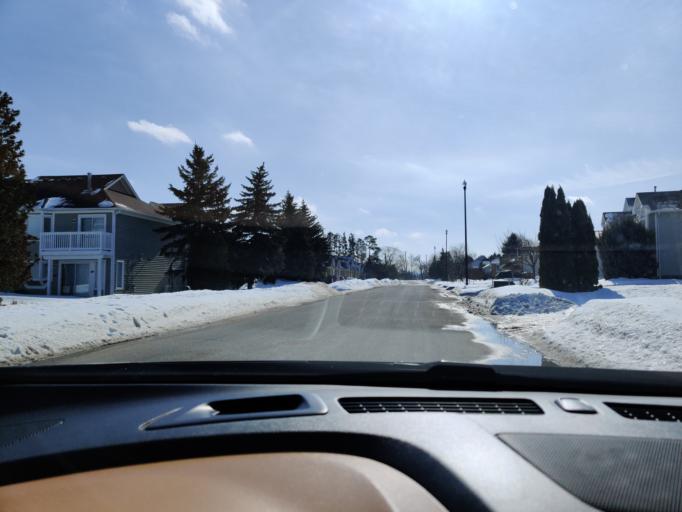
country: CA
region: Ontario
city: Collingwood
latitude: 44.5116
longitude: -80.2368
